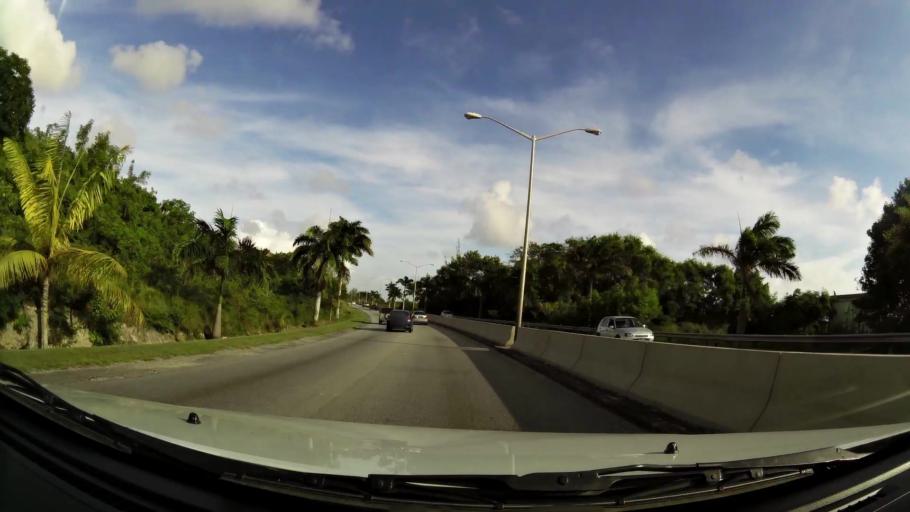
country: BB
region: Christ Church
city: Oistins
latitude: 13.0811
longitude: -59.5757
